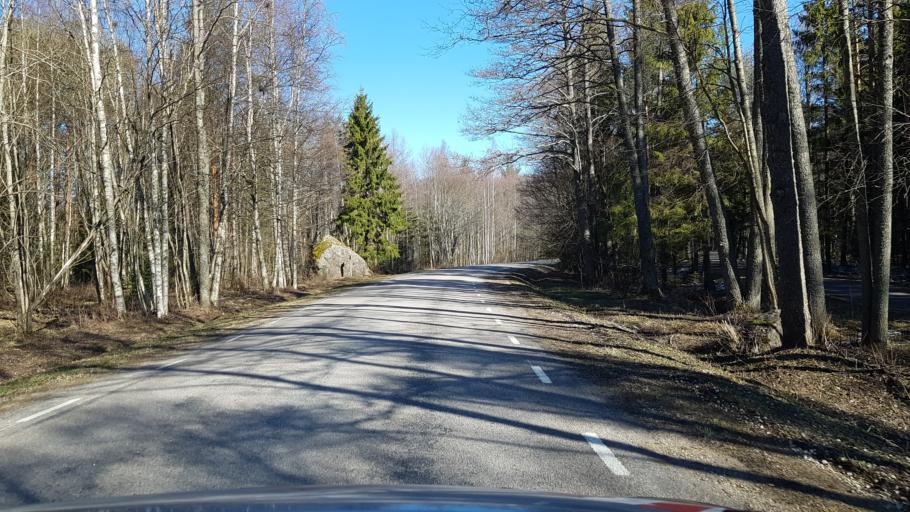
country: EE
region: Harju
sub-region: Loksa linn
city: Loksa
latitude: 59.5914
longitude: 25.9091
